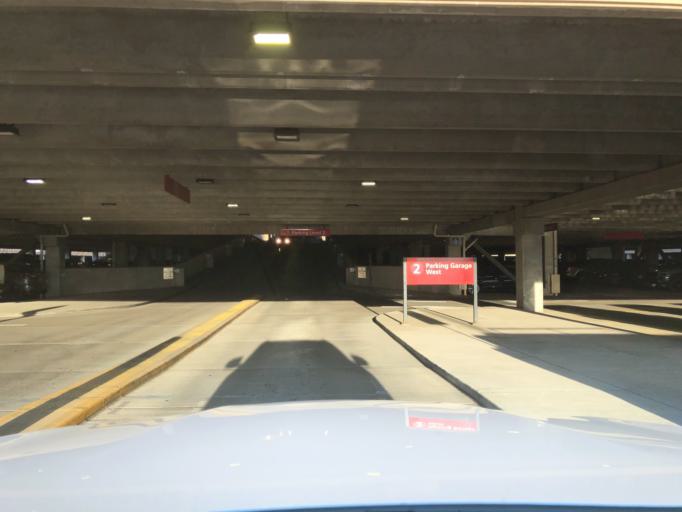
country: US
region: Colorado
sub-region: Weld County
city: Lochbuie
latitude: 39.8494
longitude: -104.6775
